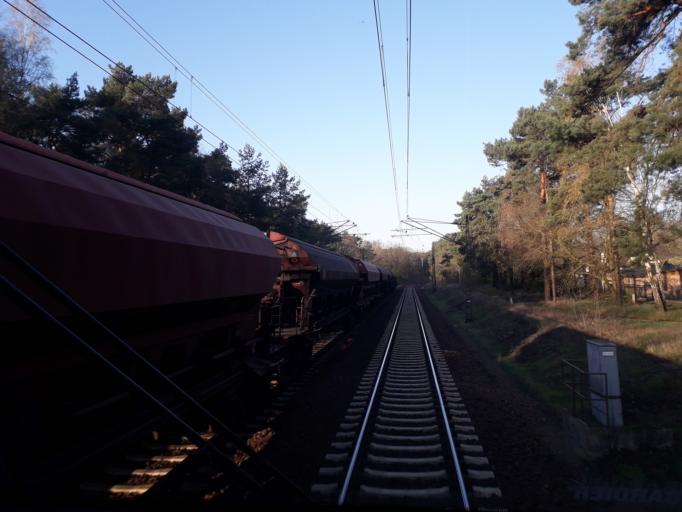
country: DE
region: Brandenburg
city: Ludwigsfelde
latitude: 52.3194
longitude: 13.2389
